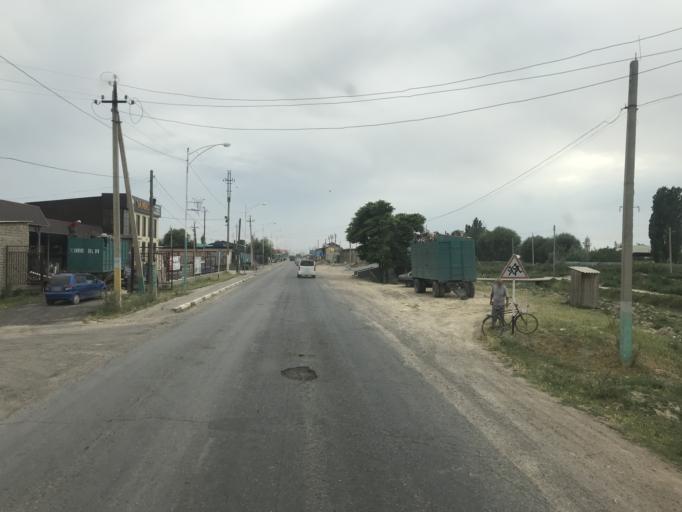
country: KZ
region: Ongtustik Qazaqstan
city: Asykata
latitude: 40.9033
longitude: 68.3625
